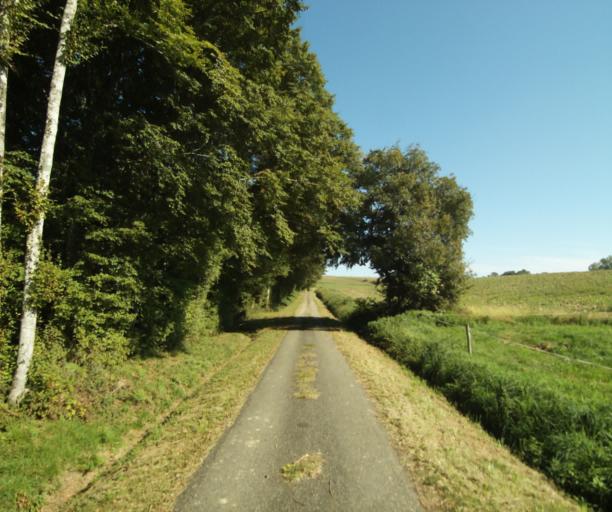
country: FR
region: Aquitaine
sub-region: Departement des Landes
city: Gabarret
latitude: 43.9450
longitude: -0.0030
